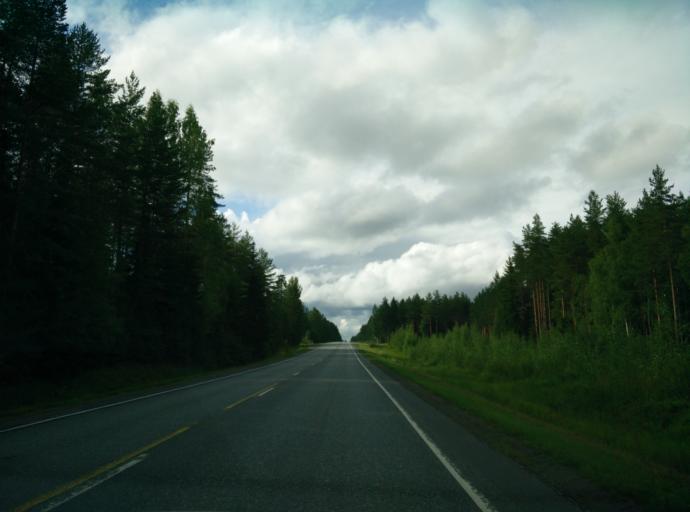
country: FI
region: Haeme
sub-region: Haemeenlinna
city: Kalvola
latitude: 61.1080
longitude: 24.1319
